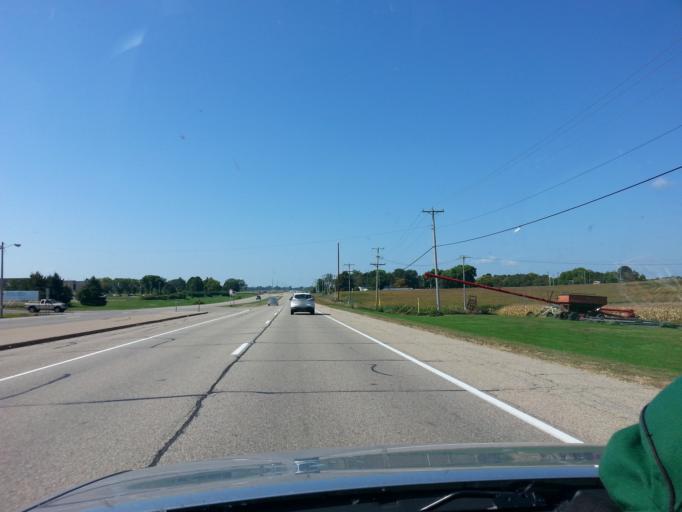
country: US
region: Minnesota
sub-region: Dakota County
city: Rosemount
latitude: 44.7391
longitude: -93.0738
